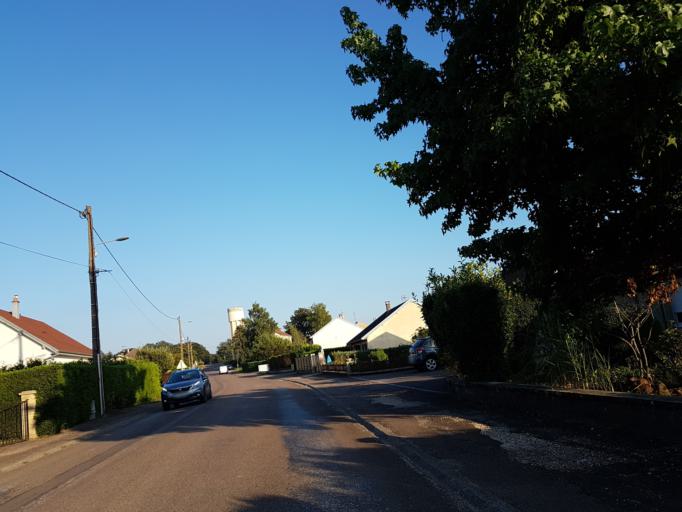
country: FR
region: Franche-Comte
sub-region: Departement de la Haute-Saone
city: Froideconche
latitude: 47.8176
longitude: 6.4231
